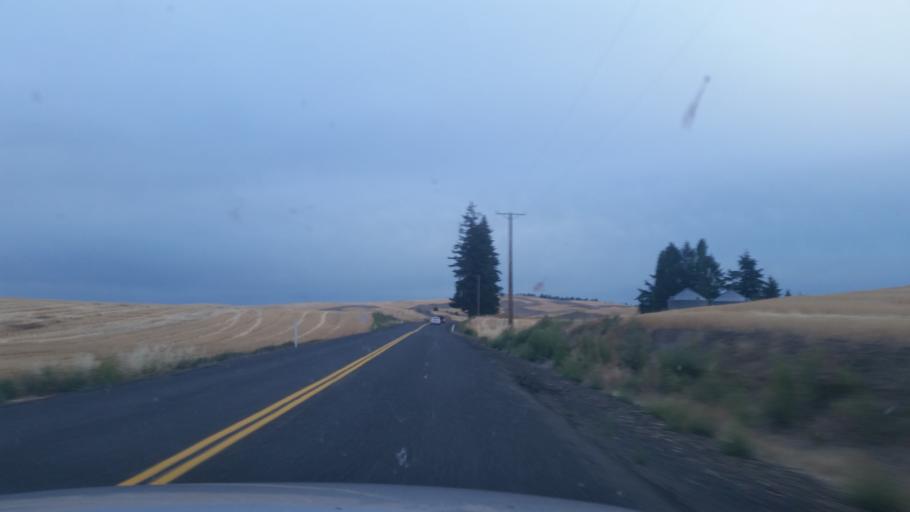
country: US
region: Washington
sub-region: Spokane County
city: Cheney
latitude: 47.5203
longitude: -117.5983
